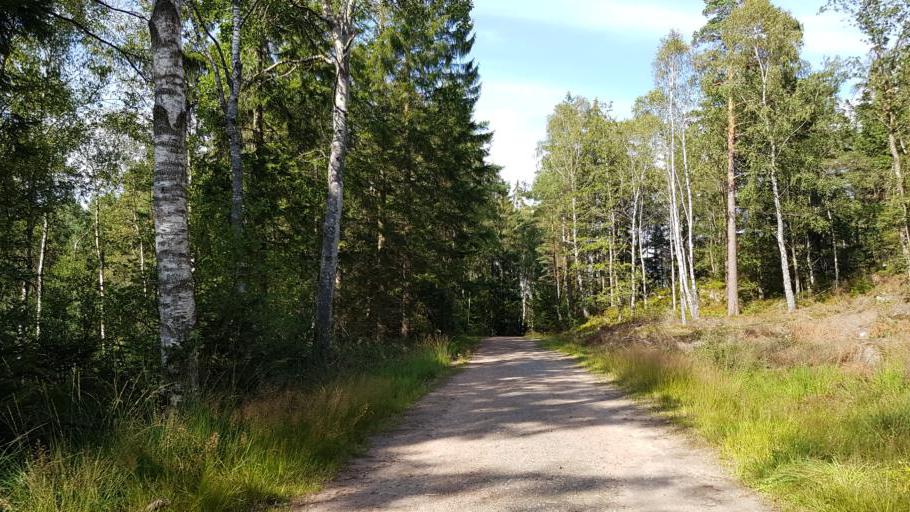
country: SE
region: Vaestra Goetaland
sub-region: Partille Kommun
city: Ojersjo
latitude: 57.6797
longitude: 12.0698
